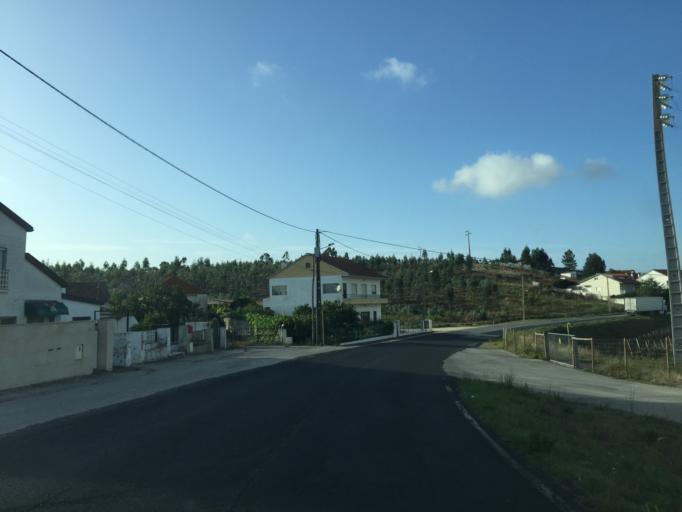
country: PT
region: Lisbon
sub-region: Torres Vedras
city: Torres Vedras
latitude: 39.1180
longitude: -9.2637
